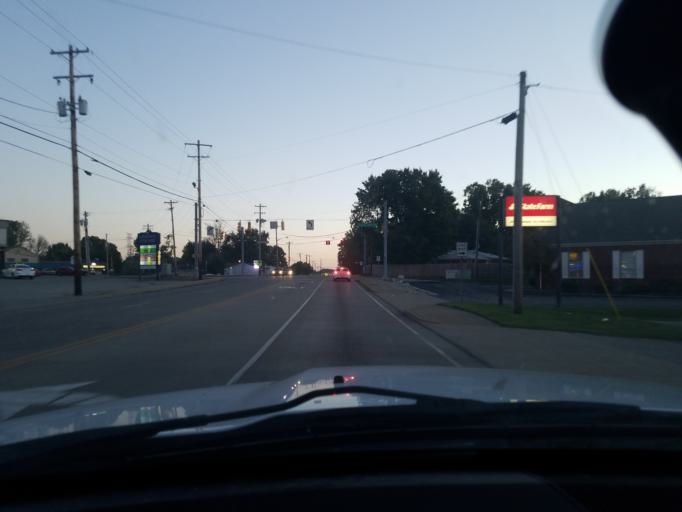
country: US
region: Indiana
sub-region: Floyd County
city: New Albany
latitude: 38.3236
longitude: -85.8016
